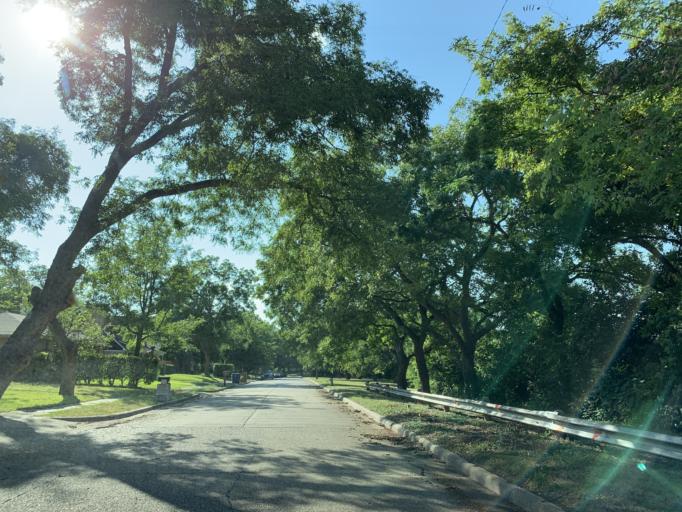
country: US
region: Texas
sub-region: Dallas County
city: Cockrell Hill
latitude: 32.6839
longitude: -96.8068
